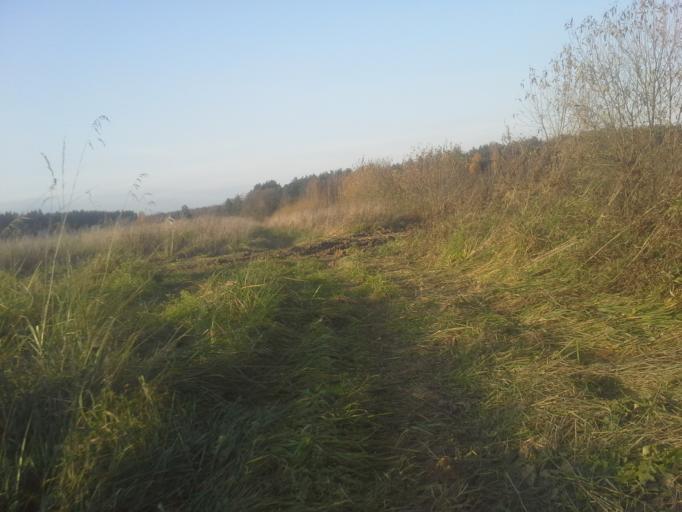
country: RU
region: Moskovskaya
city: Golitsyno
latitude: 55.5958
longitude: 37.0019
